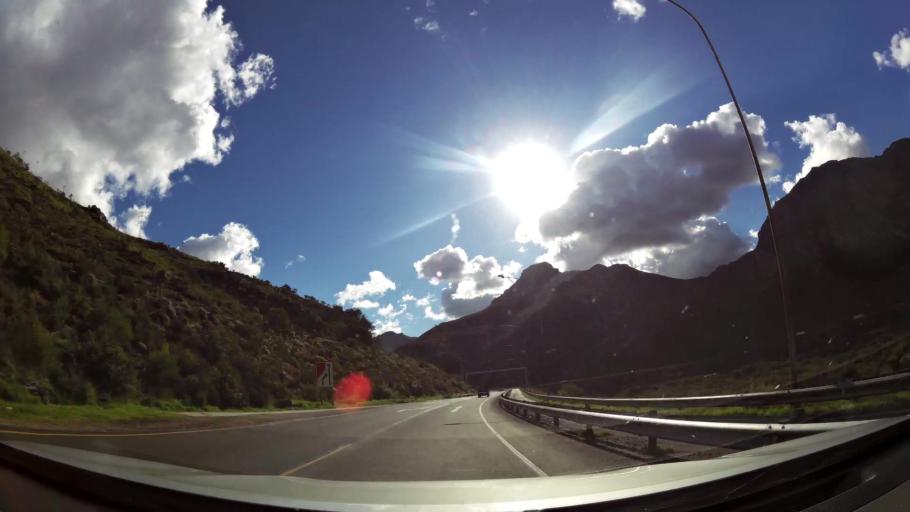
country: ZA
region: Western Cape
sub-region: Cape Winelands District Municipality
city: Paarl
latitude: -33.7329
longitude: 19.1199
